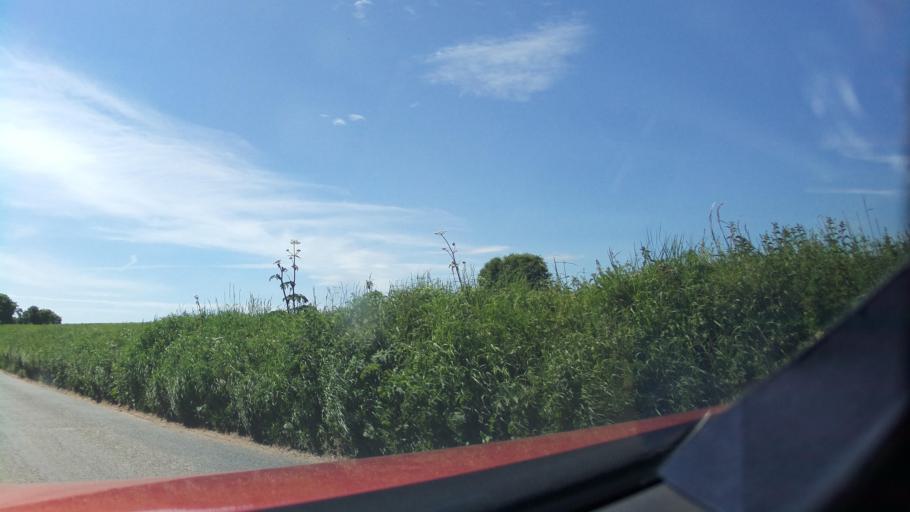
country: GB
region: England
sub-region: Devon
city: Ottery St Mary
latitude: 50.7671
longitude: -3.2645
